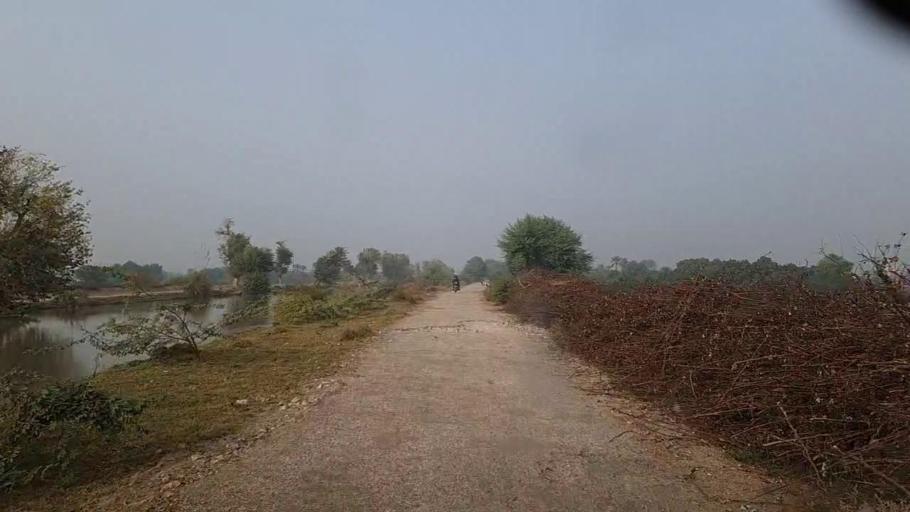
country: PK
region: Sindh
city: Bozdar
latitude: 27.1547
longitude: 68.6605
